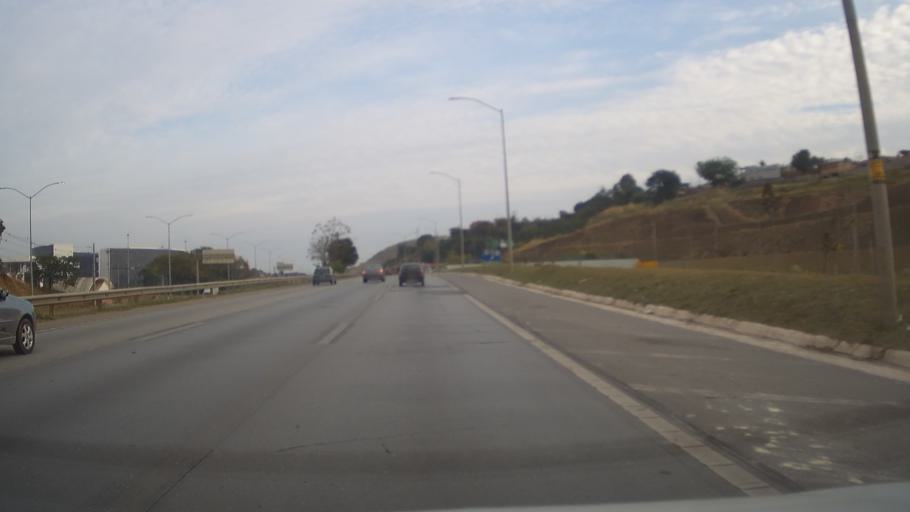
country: BR
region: Minas Gerais
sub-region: Santa Luzia
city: Santa Luzia
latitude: -19.7920
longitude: -43.9492
